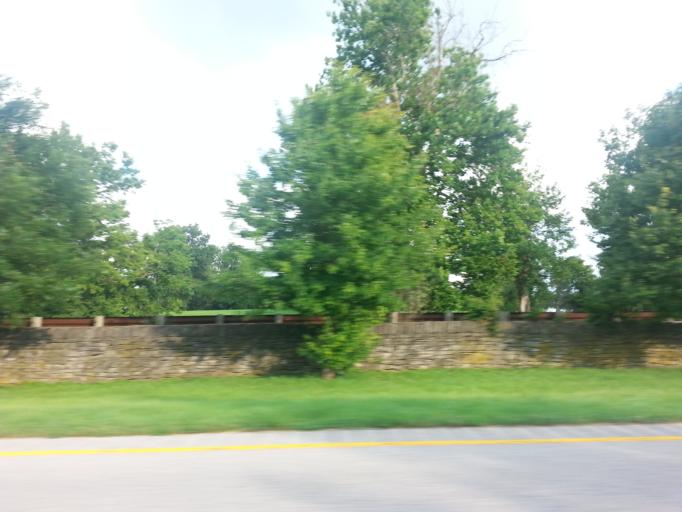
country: US
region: Kentucky
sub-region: Fayette County
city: Lexington-Fayette
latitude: 38.1168
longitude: -84.3940
